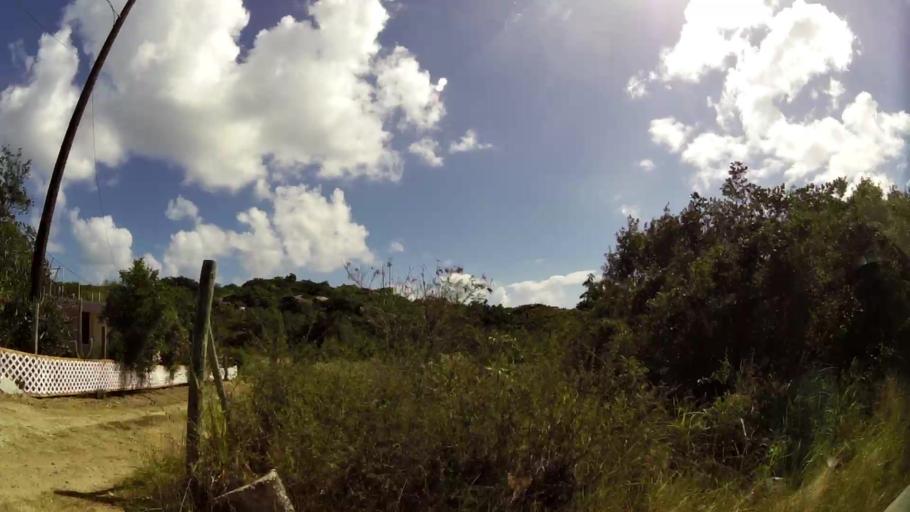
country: VG
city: Tortola
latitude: 18.4343
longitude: -64.4407
